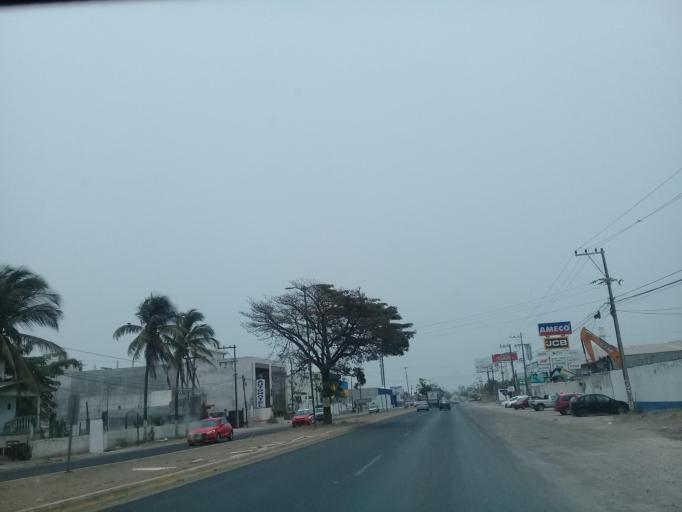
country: MX
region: Veracruz
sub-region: Veracruz
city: Las Amapolas
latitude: 19.1625
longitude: -96.2077
